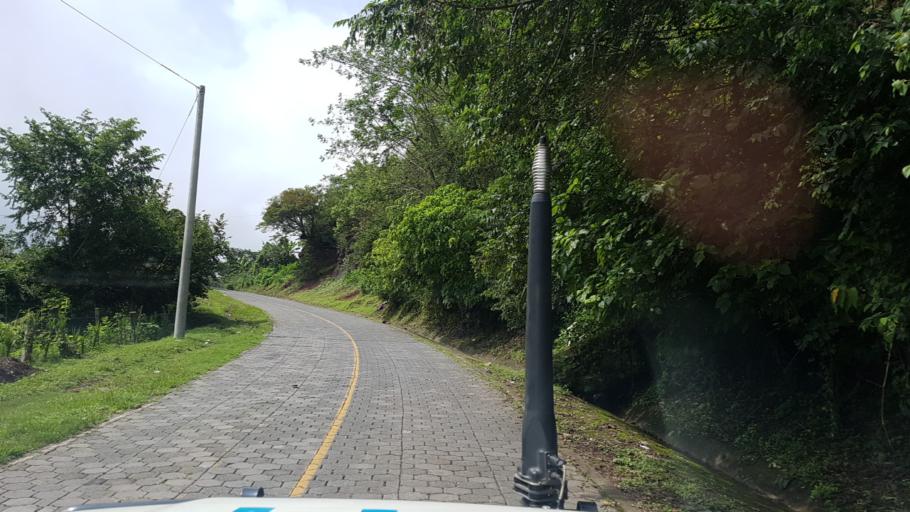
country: NI
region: Leon
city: Santa Rosa del Penon
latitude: 12.9382
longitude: -86.3388
